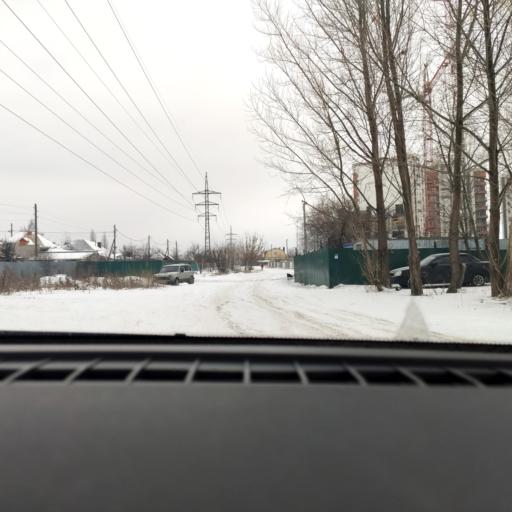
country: RU
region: Voronezj
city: Maslovka
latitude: 51.6123
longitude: 39.2185
